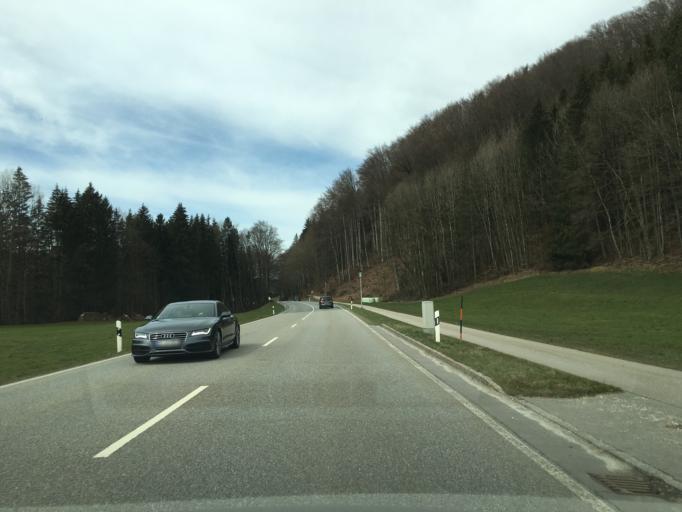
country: DE
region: Bavaria
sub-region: Upper Bavaria
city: Inzell
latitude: 47.7971
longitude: 12.7172
